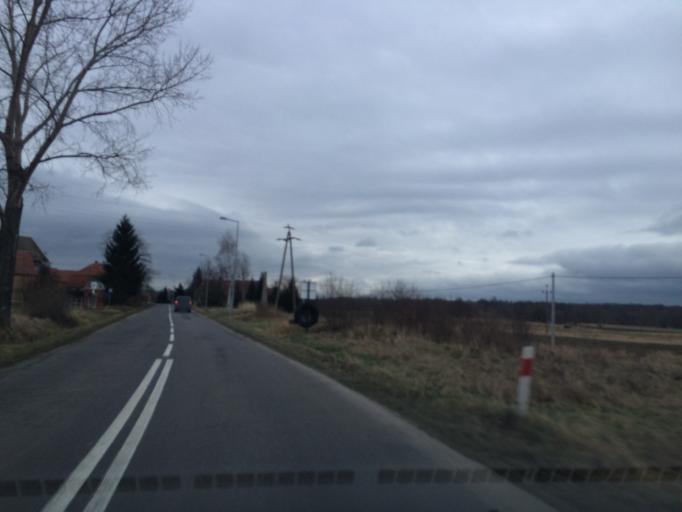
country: PL
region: Lower Silesian Voivodeship
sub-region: Powiat boleslawiecki
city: Nowogrodziec
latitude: 51.1889
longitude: 15.3652
